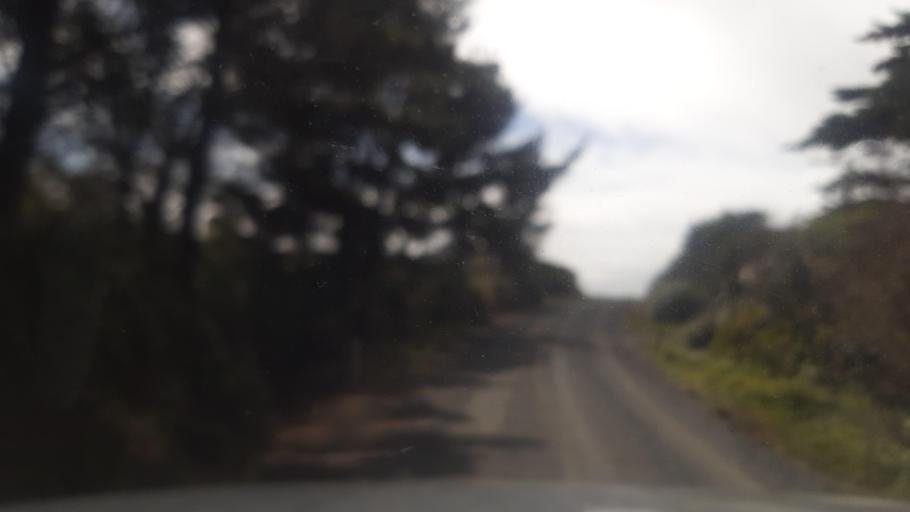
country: NZ
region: Northland
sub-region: Far North District
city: Kaitaia
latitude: -34.7414
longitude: 173.1145
